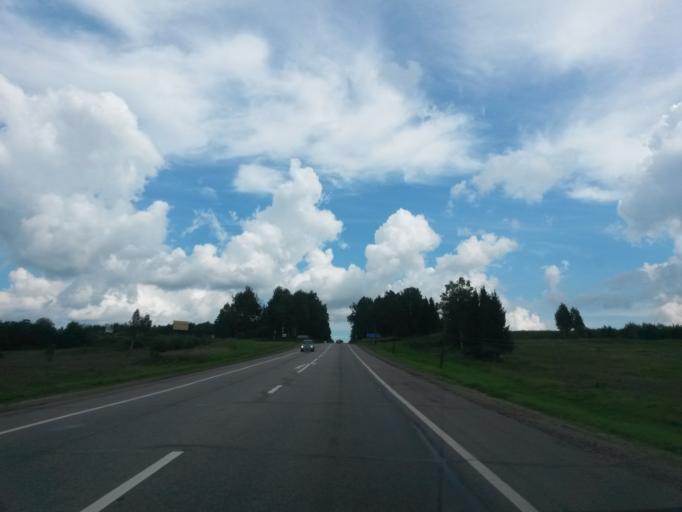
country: RU
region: Vladimir
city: Balakirevo
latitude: 56.6234
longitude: 38.6595
